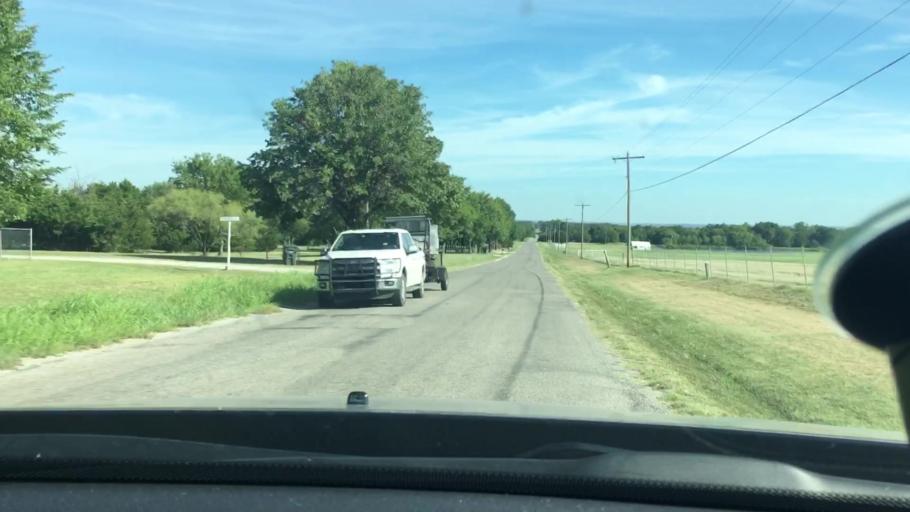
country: US
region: Oklahoma
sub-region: Carter County
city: Lone Grove
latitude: 34.2258
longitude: -97.2474
